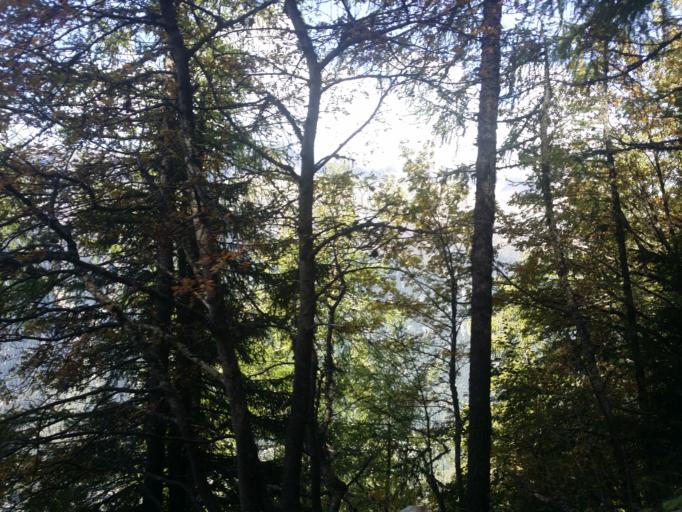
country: FR
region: Rhone-Alpes
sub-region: Departement de la Haute-Savoie
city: Chamonix-Mont-Blanc
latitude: 45.9337
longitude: 6.9120
